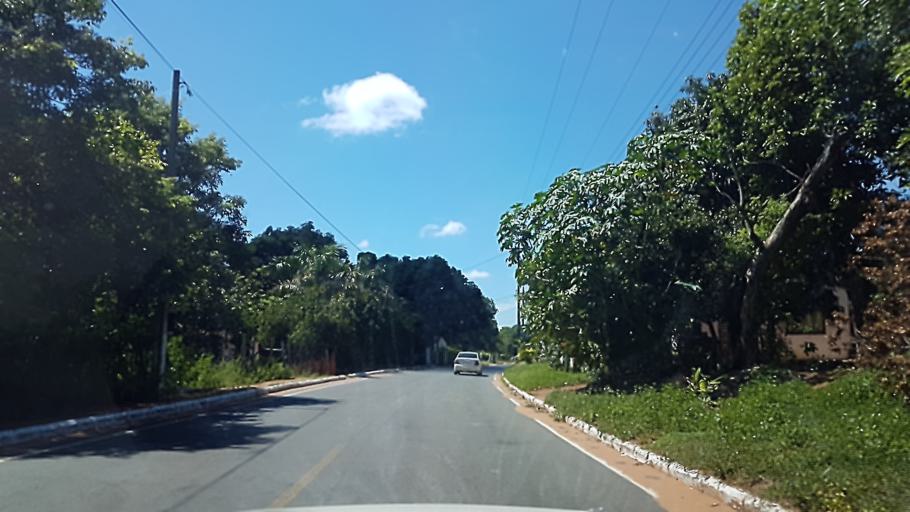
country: PY
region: Central
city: Capiata
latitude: -25.3361
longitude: -57.4311
